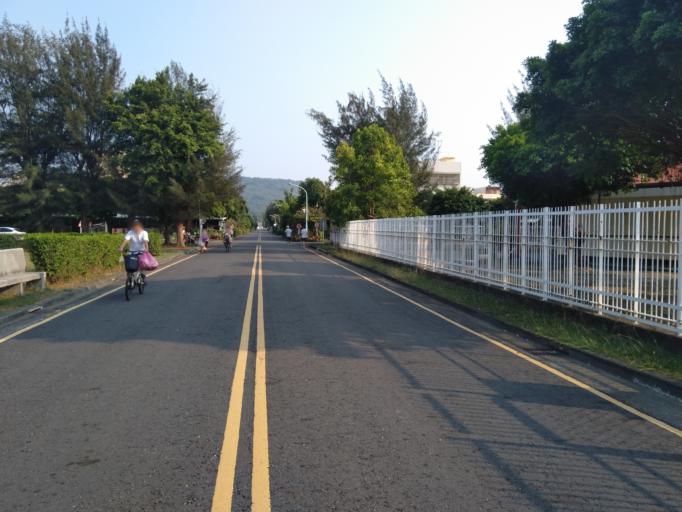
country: TW
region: Kaohsiung
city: Kaohsiung
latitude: 22.7144
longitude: 120.3043
